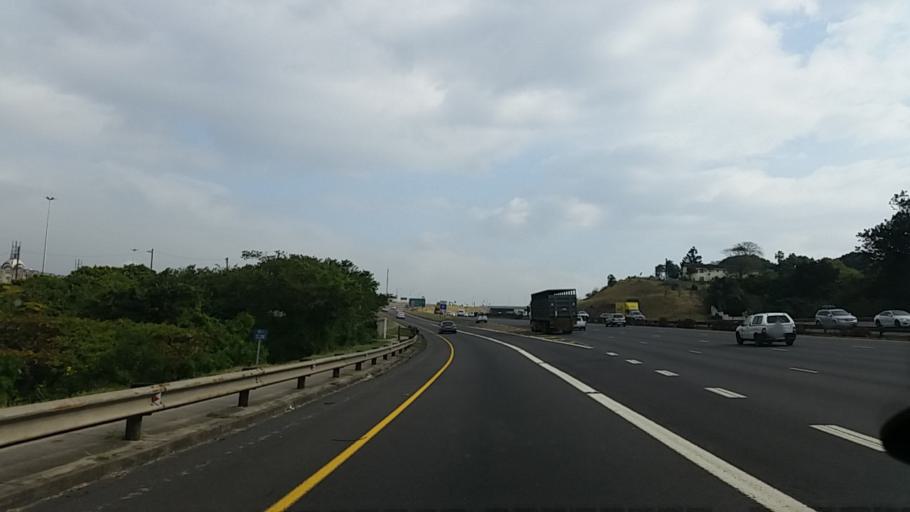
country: ZA
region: KwaZulu-Natal
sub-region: eThekwini Metropolitan Municipality
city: Berea
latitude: -29.8463
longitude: 30.9365
